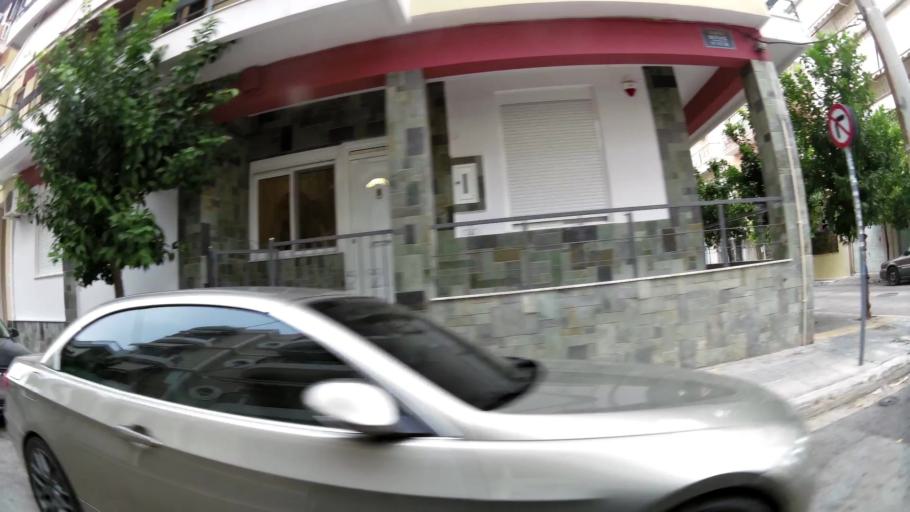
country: GR
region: Attica
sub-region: Nomos Piraios
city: Agios Ioannis Rentis
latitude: 37.9684
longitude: 23.6610
